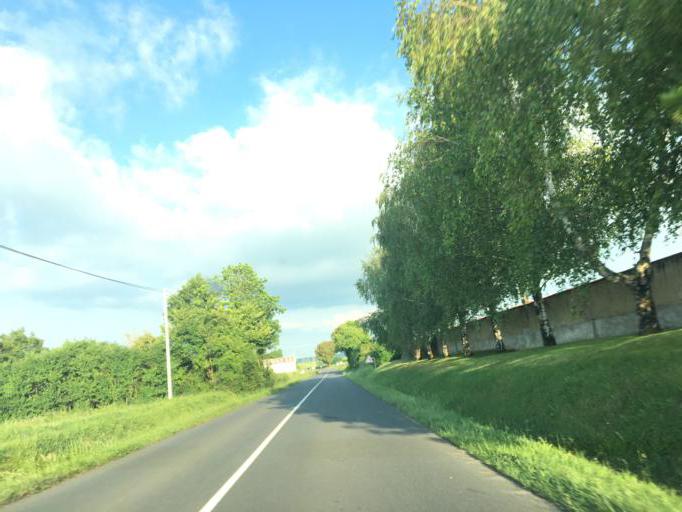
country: FR
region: Poitou-Charentes
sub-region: Departement des Deux-Sevres
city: Mauze-sur-le-Mignon
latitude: 46.0868
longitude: -0.5915
